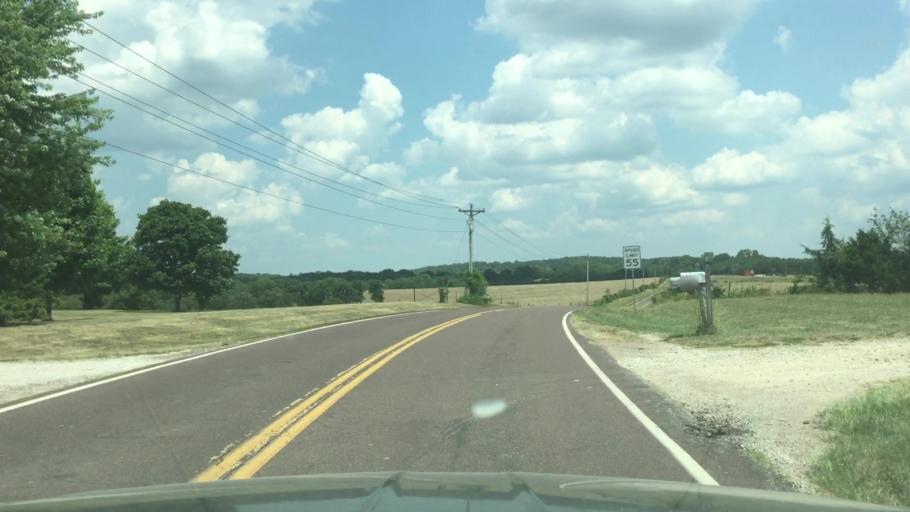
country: US
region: Missouri
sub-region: Miller County
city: Tuscumbia
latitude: 38.0963
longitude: -92.4799
